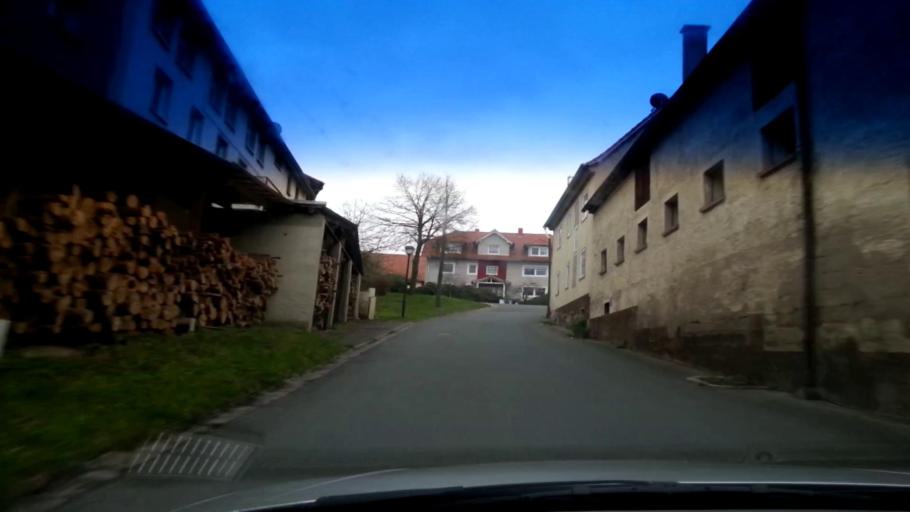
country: DE
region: Bavaria
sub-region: Upper Franconia
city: Pommersfelden
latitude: 49.8185
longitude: 10.8070
